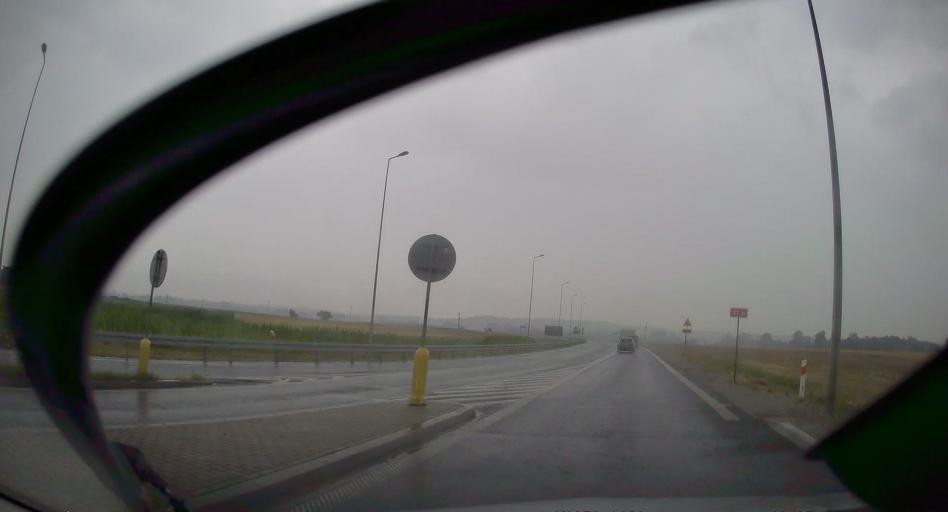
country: PL
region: Opole Voivodeship
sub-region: Powiat nyski
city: Nysa
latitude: 50.4709
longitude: 17.4070
